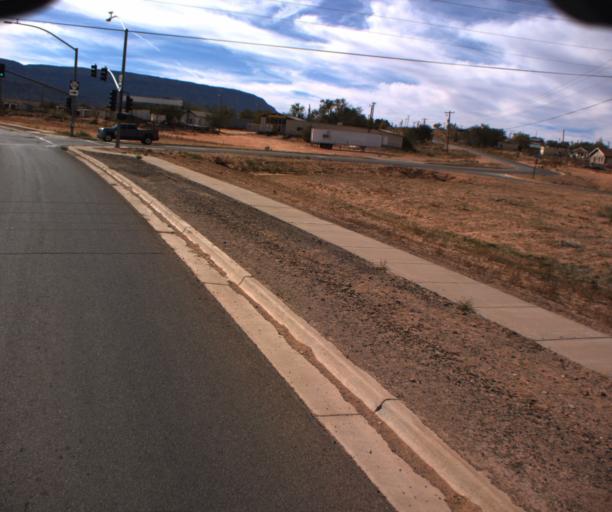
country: US
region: Arizona
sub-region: Navajo County
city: Kayenta
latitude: 36.7252
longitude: -110.2560
